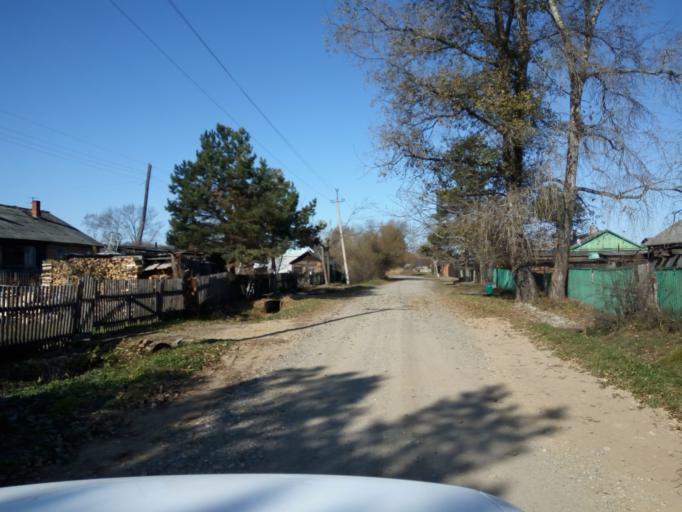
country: RU
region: Primorskiy
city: Dal'nerechensk
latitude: 45.9139
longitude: 133.8034
